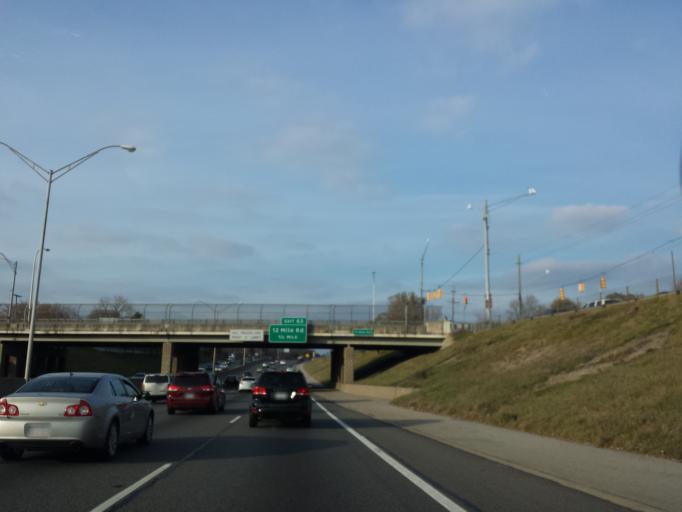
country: US
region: Michigan
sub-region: Oakland County
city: Madison Heights
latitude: 42.4899
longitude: -83.1159
